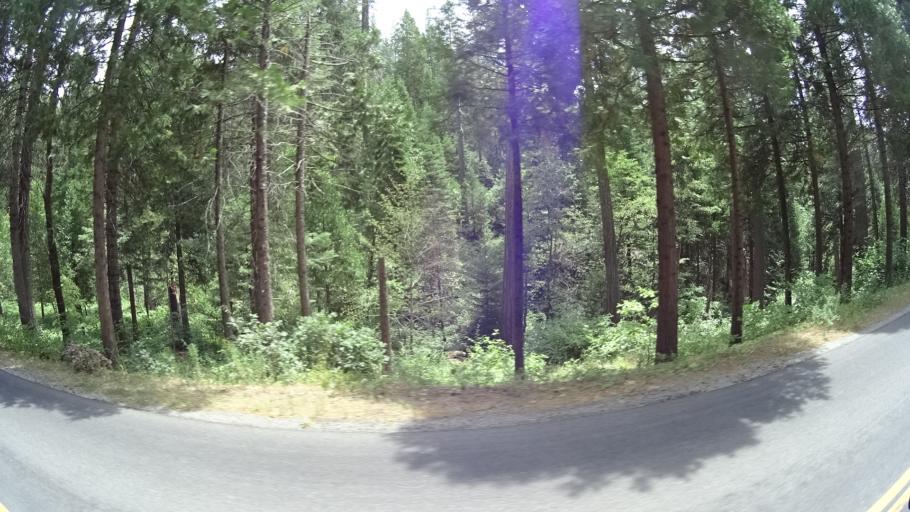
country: US
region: California
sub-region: Calaveras County
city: Arnold
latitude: 38.2408
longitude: -120.3426
